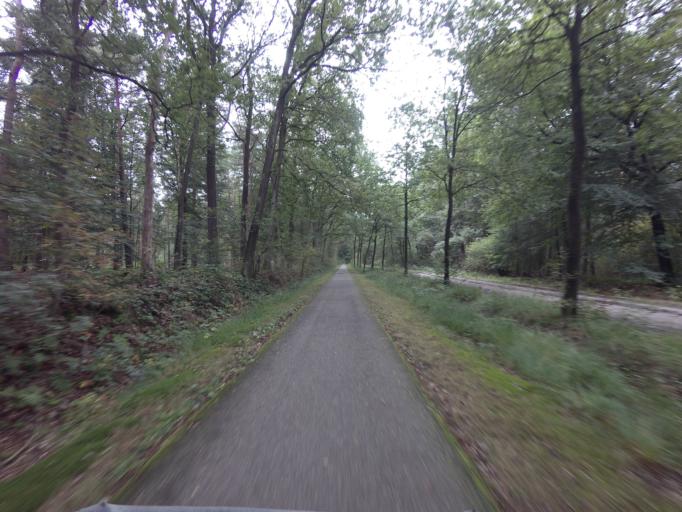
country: NL
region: Drenthe
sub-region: Gemeente Tynaarlo
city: Vries
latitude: 53.0779
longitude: 6.4660
